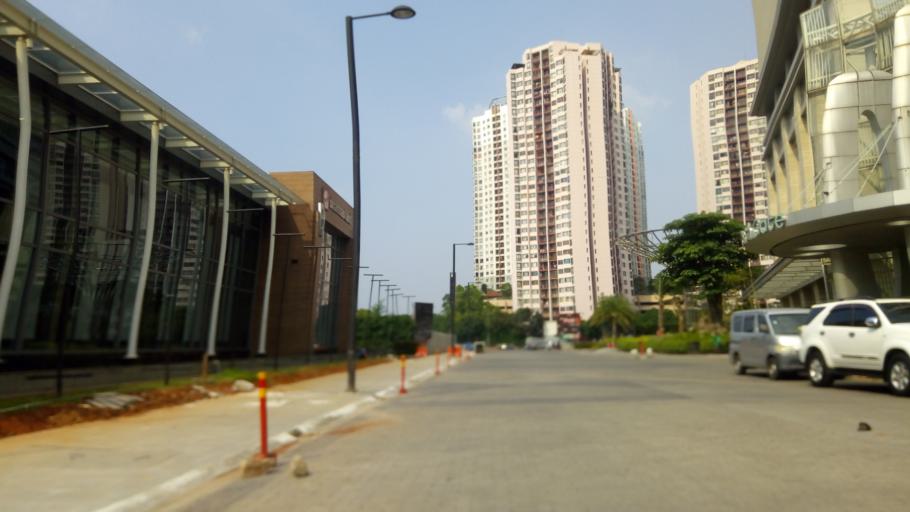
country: ID
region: Jakarta Raya
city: Jakarta
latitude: -6.2162
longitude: 106.8348
